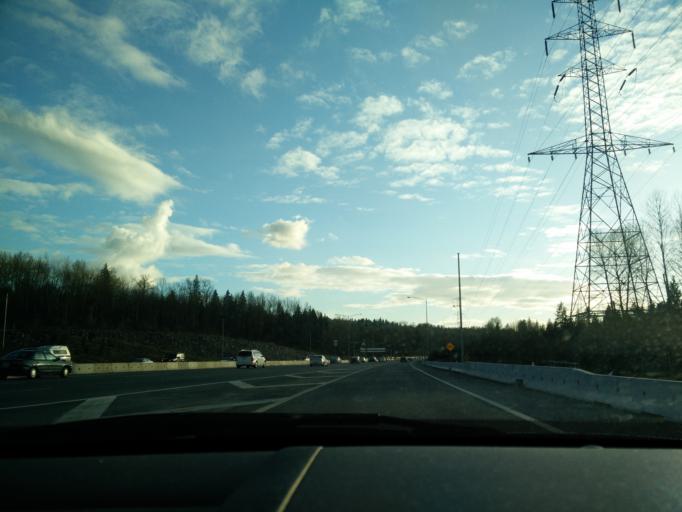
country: CA
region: British Columbia
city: New Westminster
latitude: 49.2424
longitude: -122.9161
